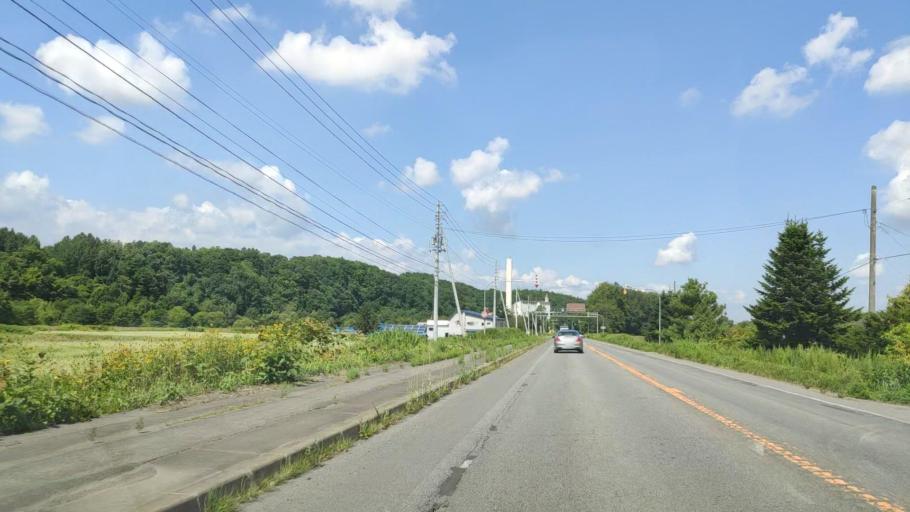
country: JP
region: Hokkaido
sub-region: Asahikawa-shi
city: Asahikawa
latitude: 43.6185
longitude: 142.4741
